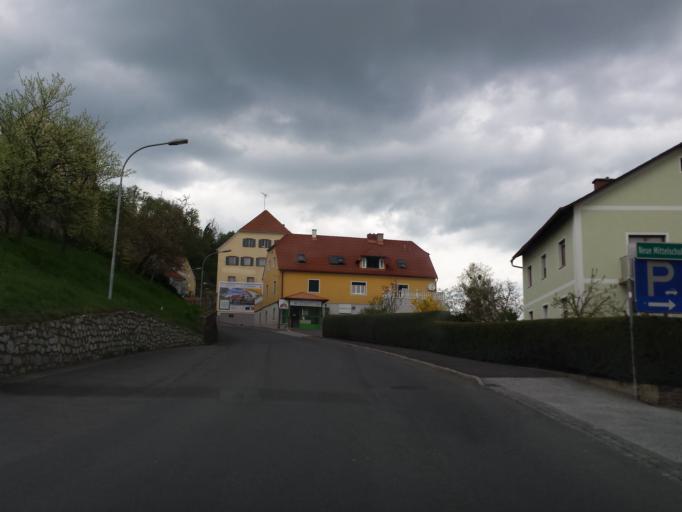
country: AT
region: Styria
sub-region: Politischer Bezirk Suedoststeiermark
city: Riegersburg
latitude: 47.0002
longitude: 15.9374
